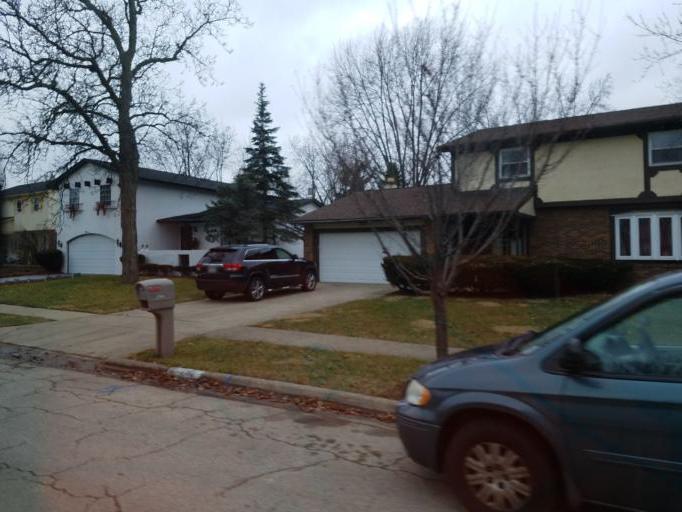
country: US
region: Ohio
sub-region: Franklin County
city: Minerva Park
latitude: 40.0769
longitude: -82.9592
